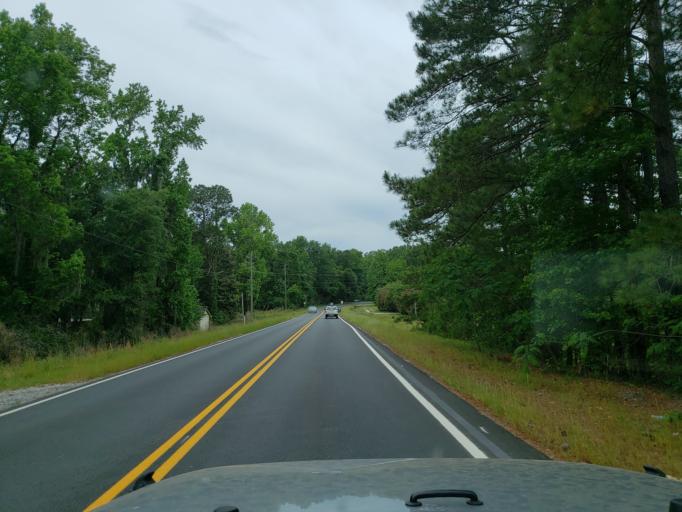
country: US
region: Georgia
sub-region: Chatham County
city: Port Wentworth
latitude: 32.1803
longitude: -81.2062
